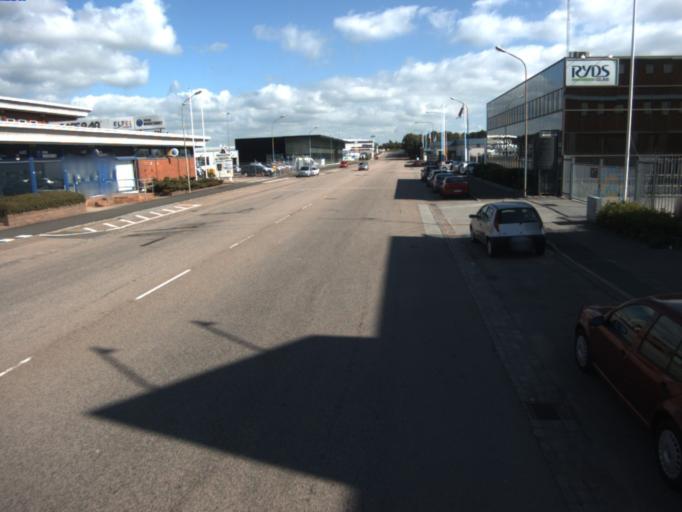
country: SE
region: Skane
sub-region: Helsingborg
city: Odakra
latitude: 56.0728
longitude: 12.7149
